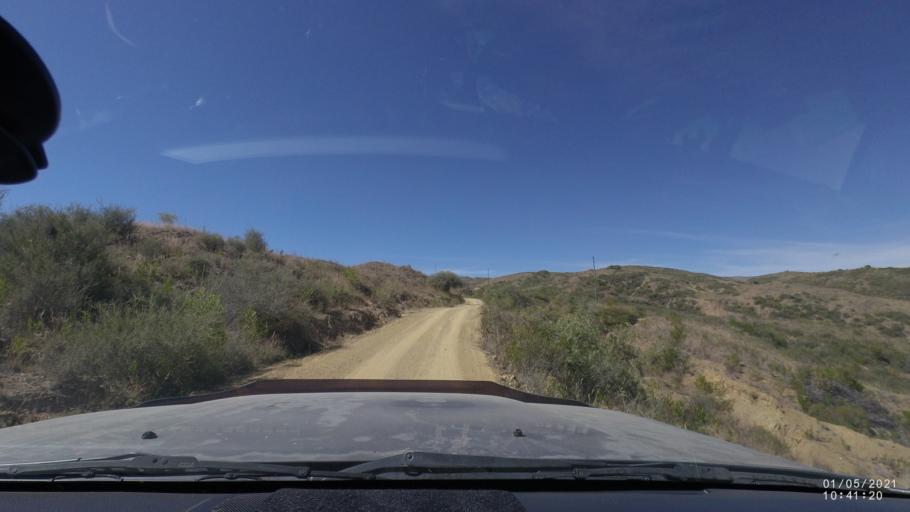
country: BO
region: Cochabamba
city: Capinota
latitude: -17.6078
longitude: -66.1778
